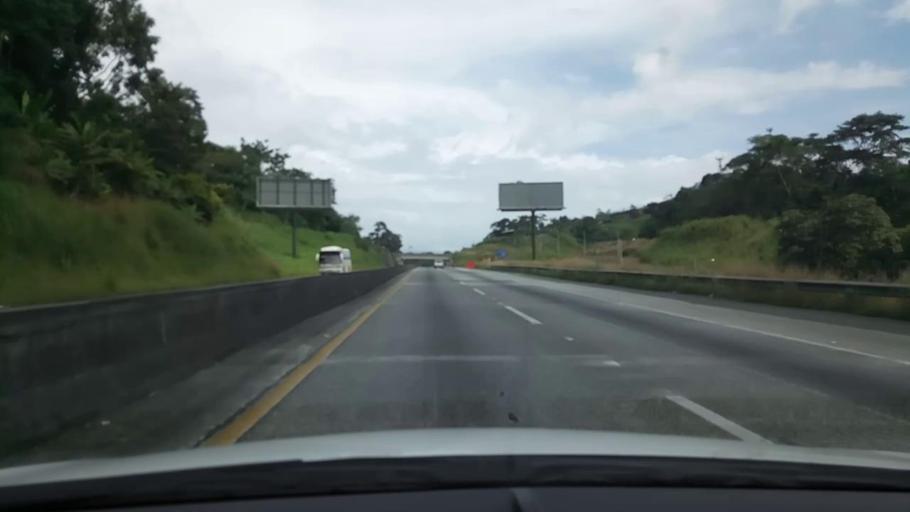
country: PA
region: Colon
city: Gatun
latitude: 9.2839
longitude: -79.7407
